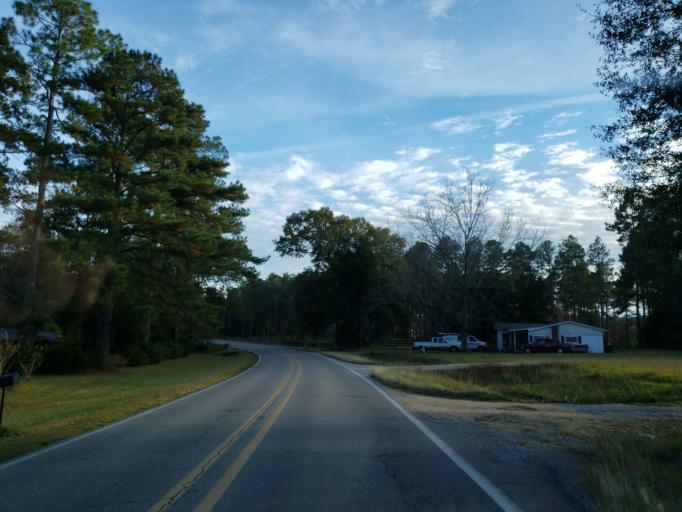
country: US
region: Mississippi
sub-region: Lamar County
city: Purvis
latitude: 31.1756
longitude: -89.4329
